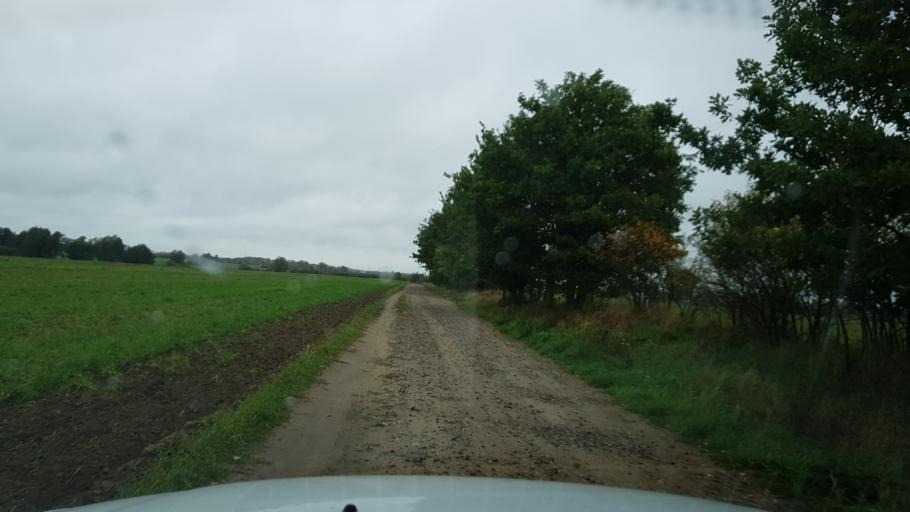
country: PL
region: West Pomeranian Voivodeship
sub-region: Powiat pyrzycki
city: Lipiany
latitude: 52.9790
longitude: 15.0074
